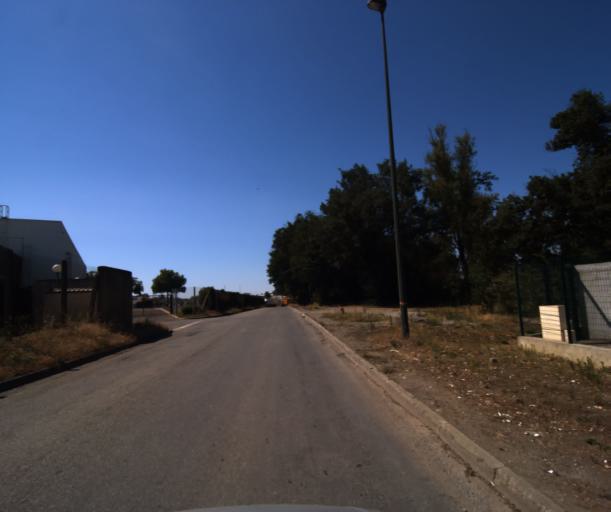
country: FR
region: Midi-Pyrenees
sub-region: Departement de la Haute-Garonne
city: Saubens
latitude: 43.4827
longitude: 1.3404
